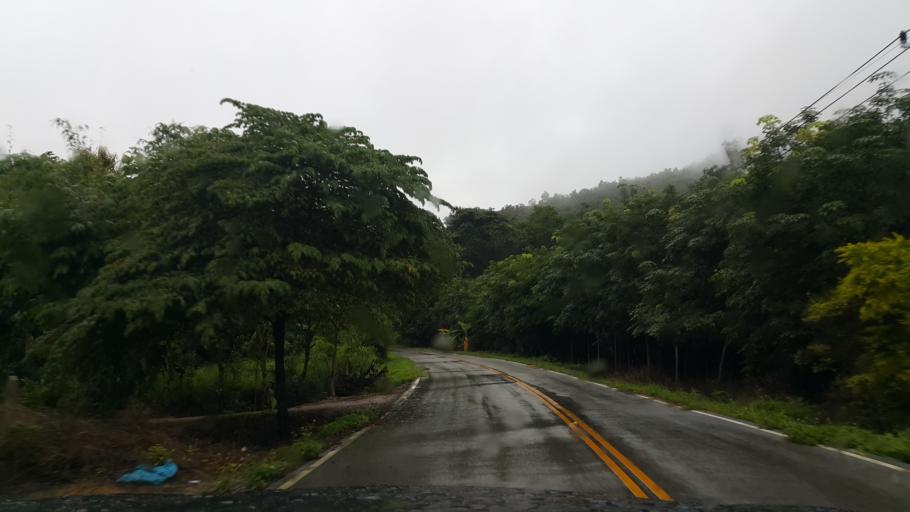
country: TH
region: Phayao
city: Phu Sang
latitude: 19.6069
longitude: 100.4070
